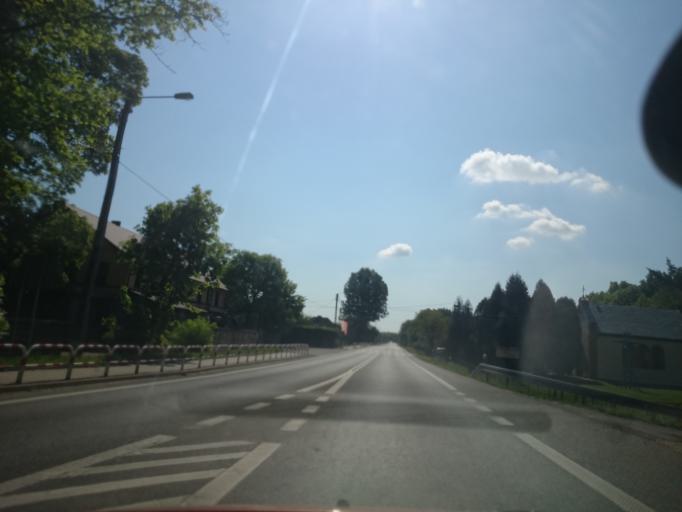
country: PL
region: Opole Voivodeship
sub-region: Powiat opolski
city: Tarnow Opolski
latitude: 50.6043
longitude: 18.0759
